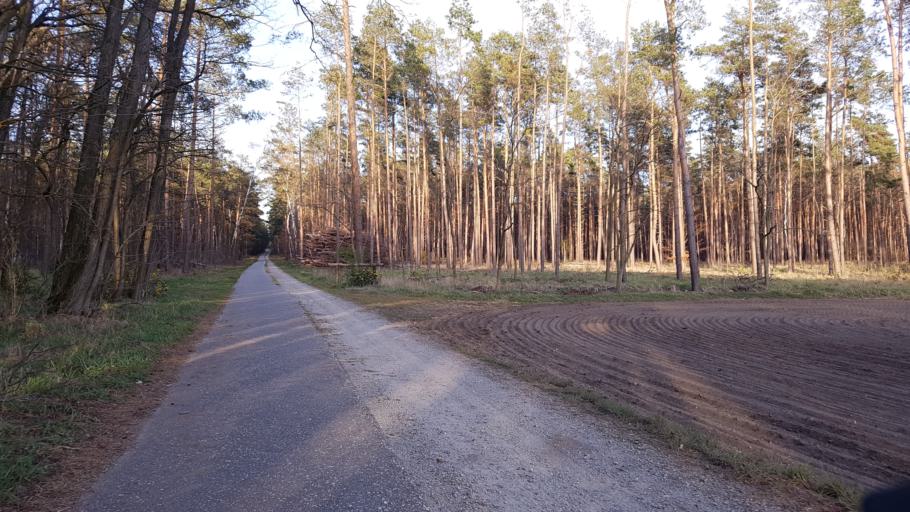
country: DE
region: Brandenburg
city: Schilda
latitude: 51.6089
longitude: 13.4059
